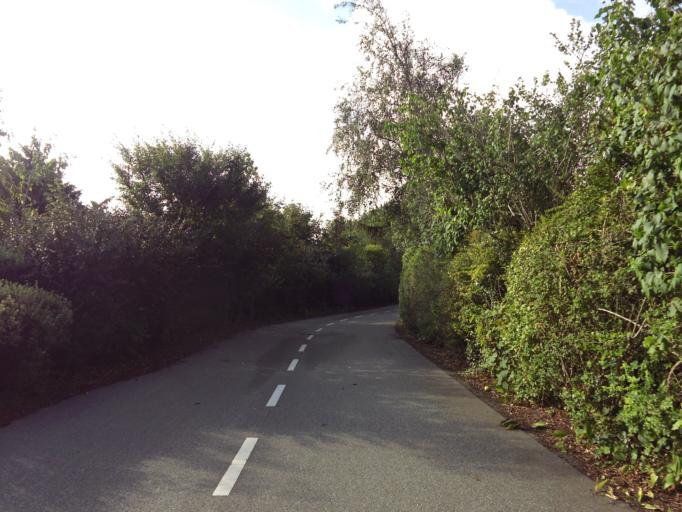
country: DK
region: South Denmark
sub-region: Esbjerg Kommune
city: Ribe
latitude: 55.3470
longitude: 8.7842
